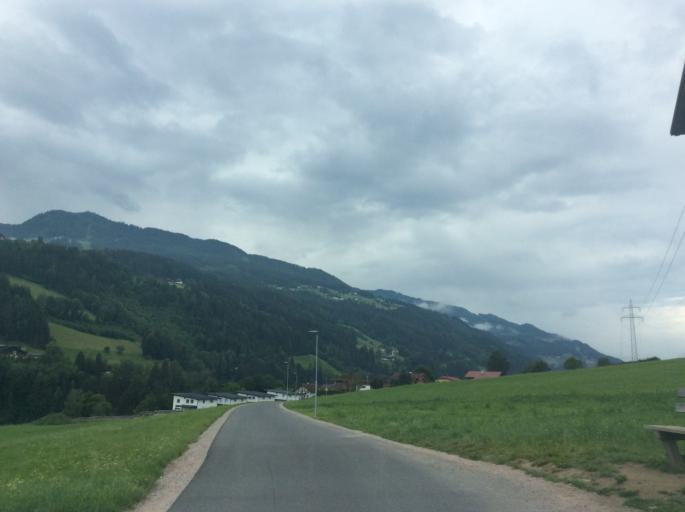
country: AT
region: Styria
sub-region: Politischer Bezirk Liezen
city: Schladming
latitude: 47.3935
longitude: 13.6692
